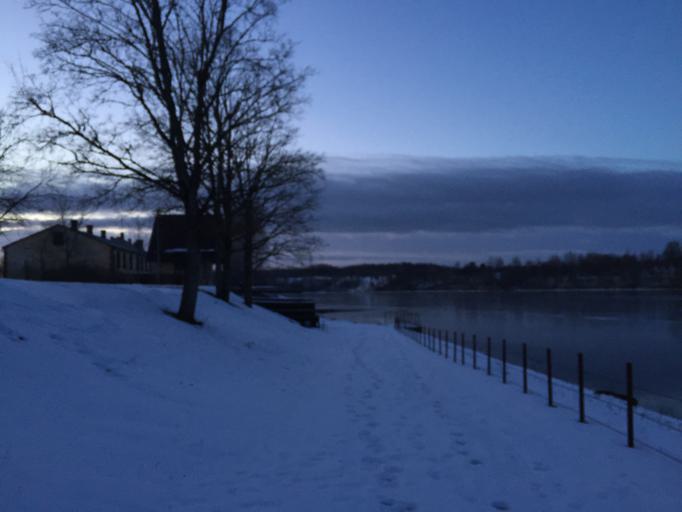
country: LV
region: Jaunjelgava
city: Jaunjelgava
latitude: 56.6208
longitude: 25.0875
